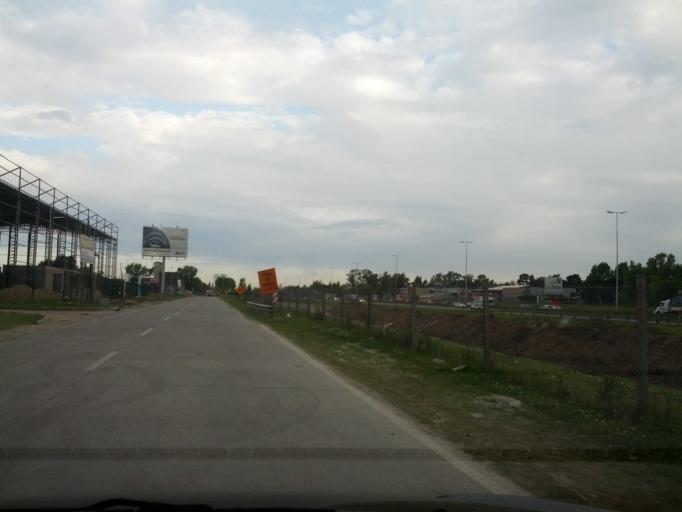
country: AR
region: Buenos Aires
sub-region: Partido de General Rodriguez
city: General Rodriguez
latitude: -34.6142
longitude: -58.8541
